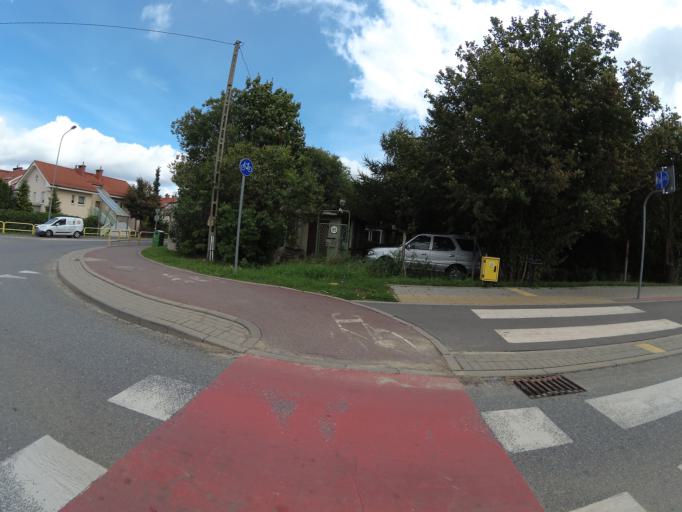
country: PL
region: Pomeranian Voivodeship
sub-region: Powiat kartuski
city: Chwaszczyno
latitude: 54.4983
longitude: 18.4388
